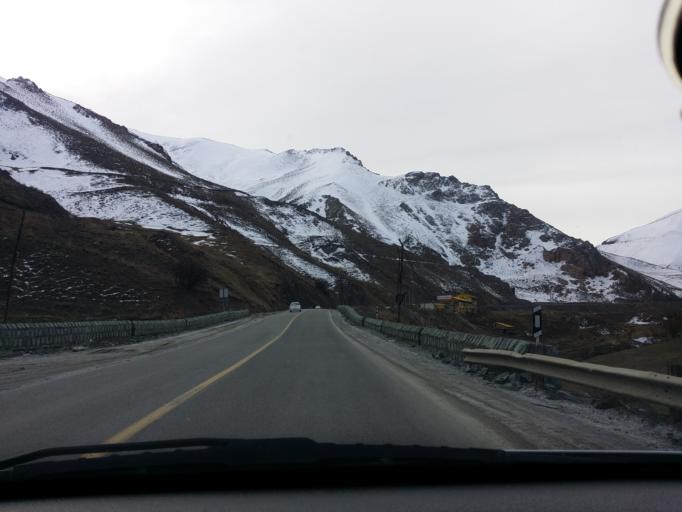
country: IR
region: Tehran
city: Tajrish
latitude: 36.1825
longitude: 51.3183
